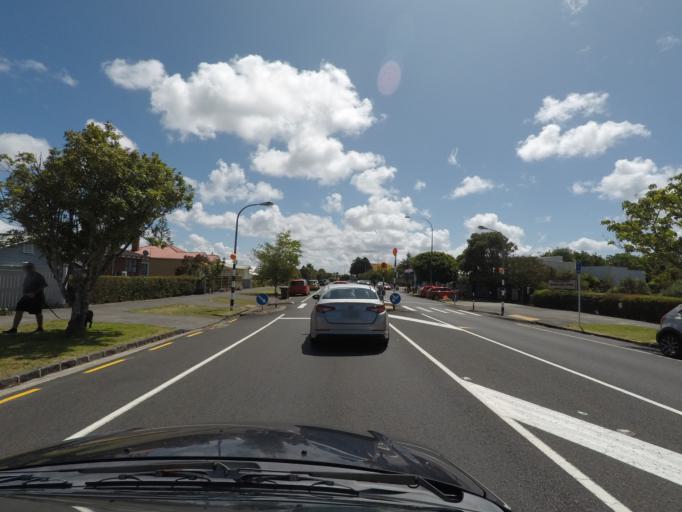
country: NZ
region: Auckland
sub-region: Auckland
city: Auckland
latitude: -36.8597
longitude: 174.7238
